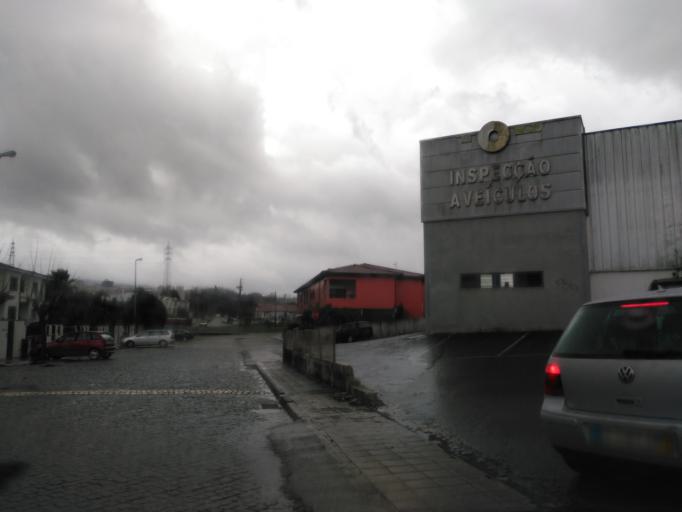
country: PT
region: Braga
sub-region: Braga
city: Braga
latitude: 41.5635
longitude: -8.4501
